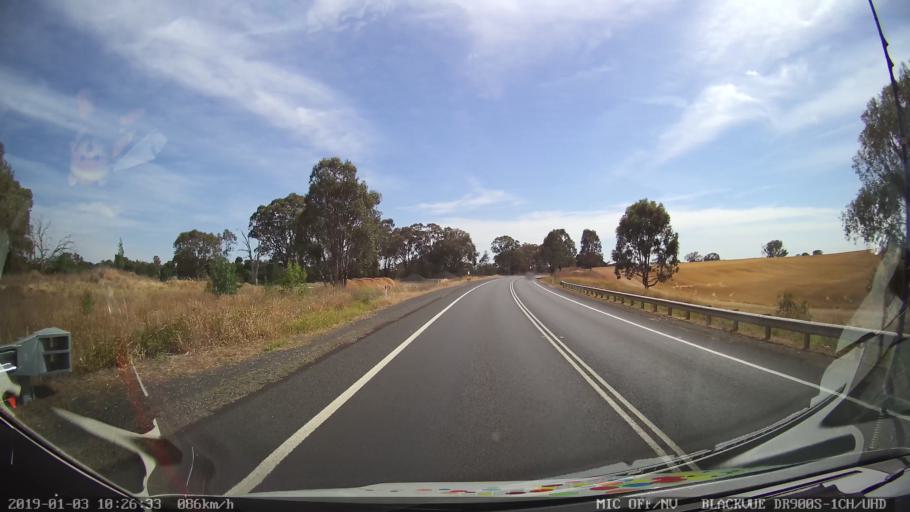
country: AU
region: New South Wales
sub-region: Young
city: Young
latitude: -34.4113
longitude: 148.2501
